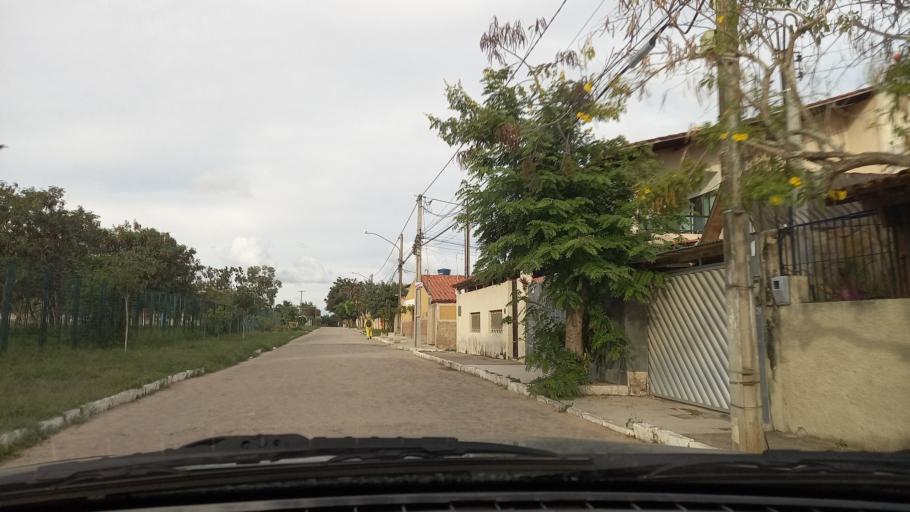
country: BR
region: Pernambuco
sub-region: Gravata
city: Gravata
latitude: -8.1980
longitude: -35.5558
